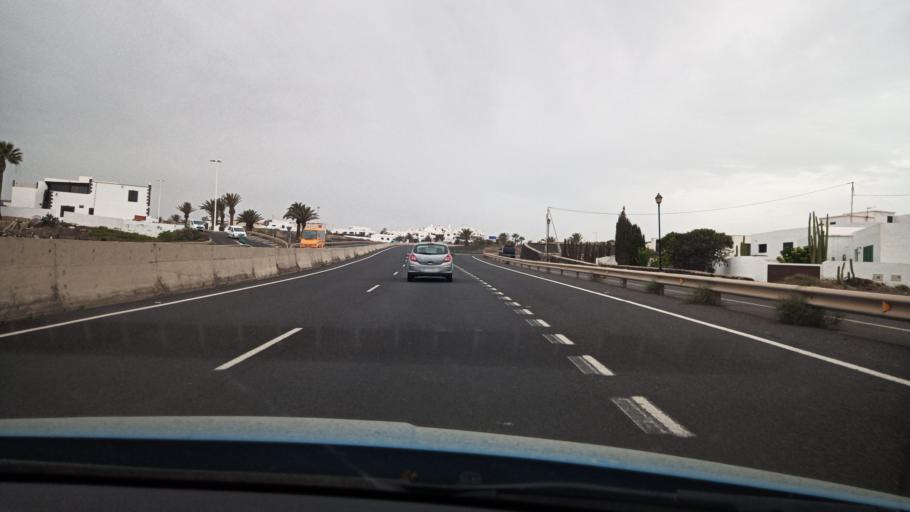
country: ES
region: Canary Islands
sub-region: Provincia de Las Palmas
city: Tias
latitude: 28.9576
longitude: -13.6453
